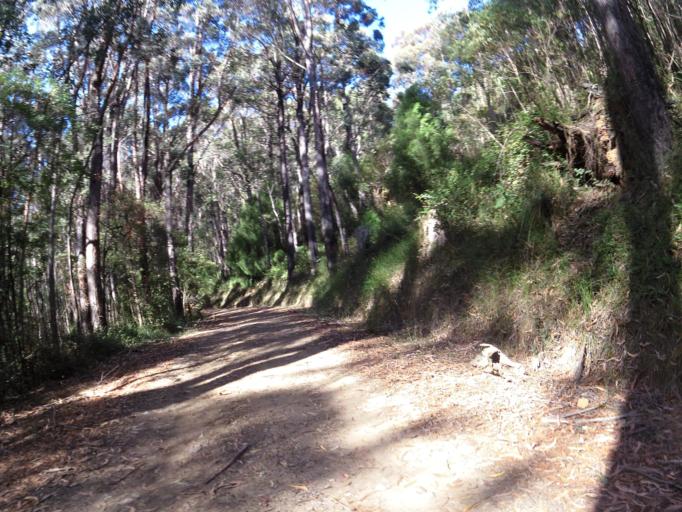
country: AU
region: Victoria
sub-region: Yarra Ranges
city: Millgrove
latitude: -37.8513
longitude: 145.7938
